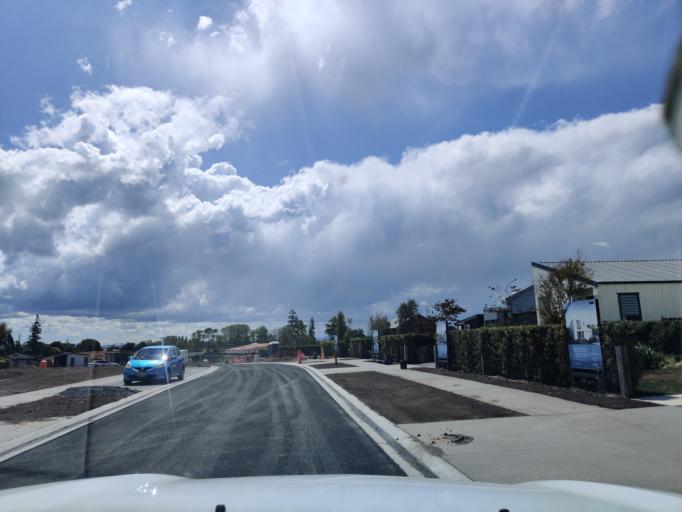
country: NZ
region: Waikato
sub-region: Waikato District
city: Te Kauwhata
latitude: -37.4146
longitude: 175.1501
